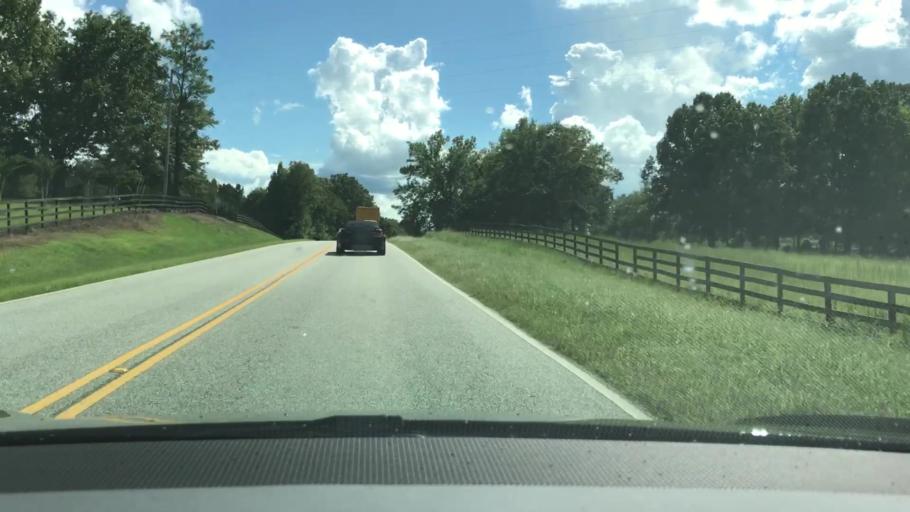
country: US
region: Alabama
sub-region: Montgomery County
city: Pike Road
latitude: 32.2135
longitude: -86.0917
